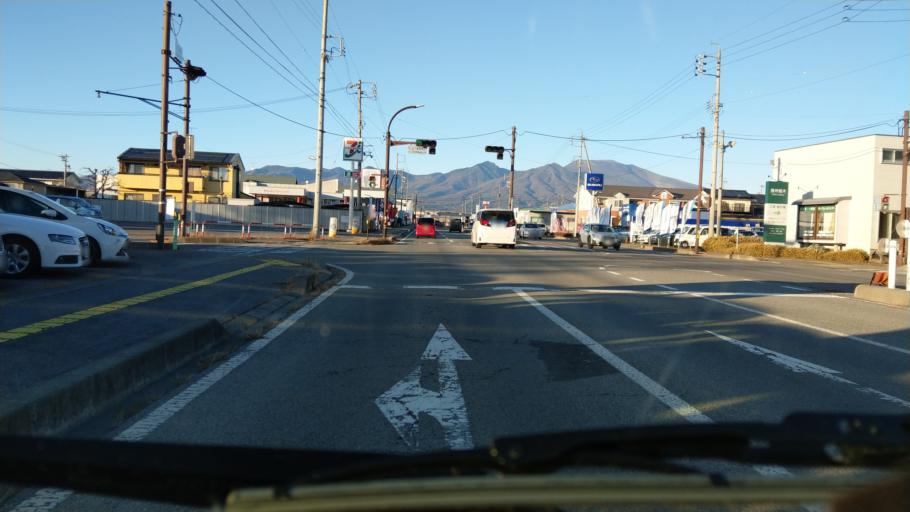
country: JP
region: Nagano
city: Saku
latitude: 36.2515
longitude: 138.4676
